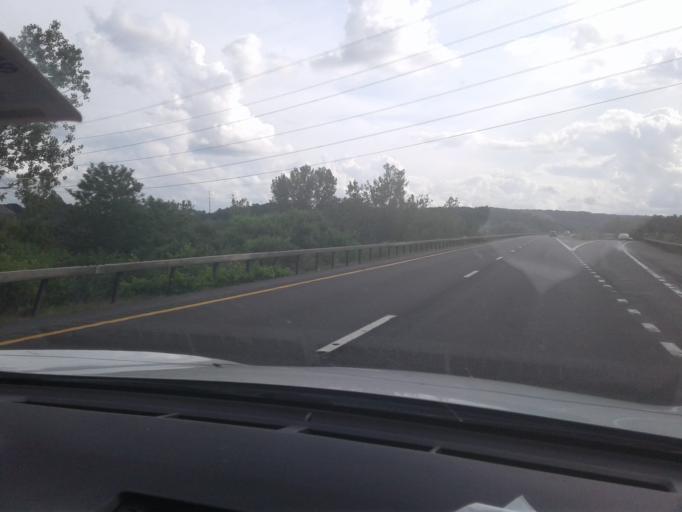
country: US
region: New York
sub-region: Onondaga County
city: East Syracuse
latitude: 43.0140
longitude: -76.0714
